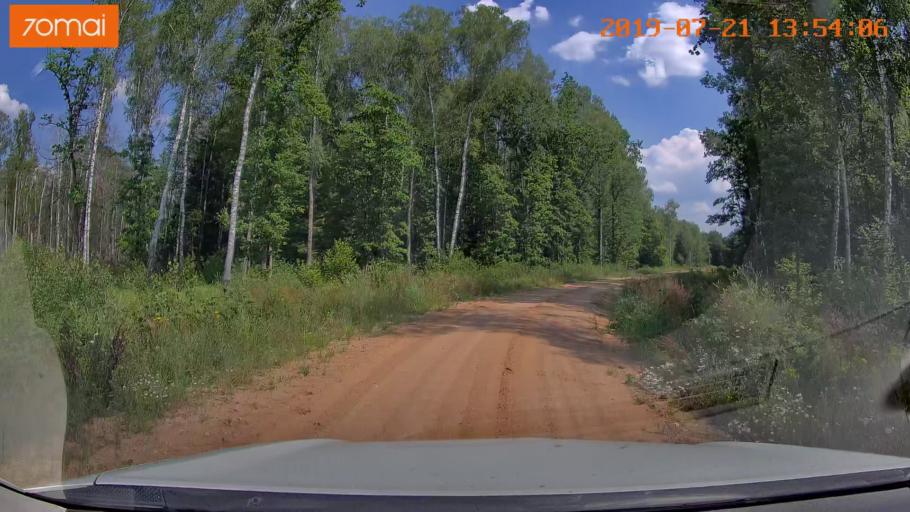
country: BY
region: Grodnenskaya
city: Lyubcha
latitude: 53.7769
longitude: 26.0695
